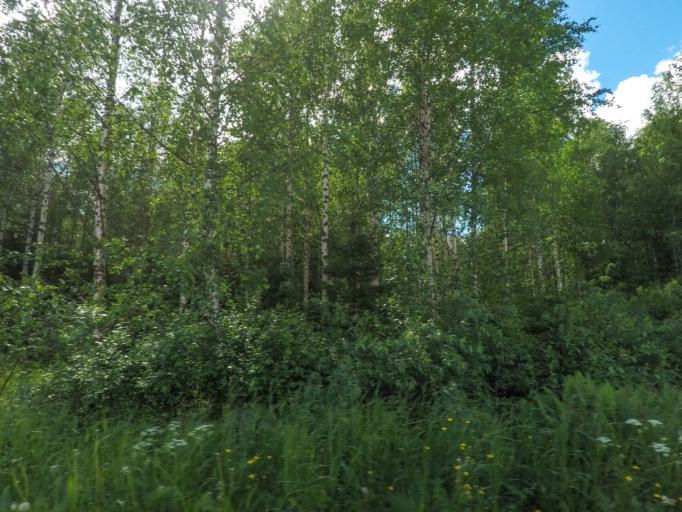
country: FI
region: Central Finland
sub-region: Jyvaeskylae
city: Hankasalmi
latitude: 62.4149
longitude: 26.6415
